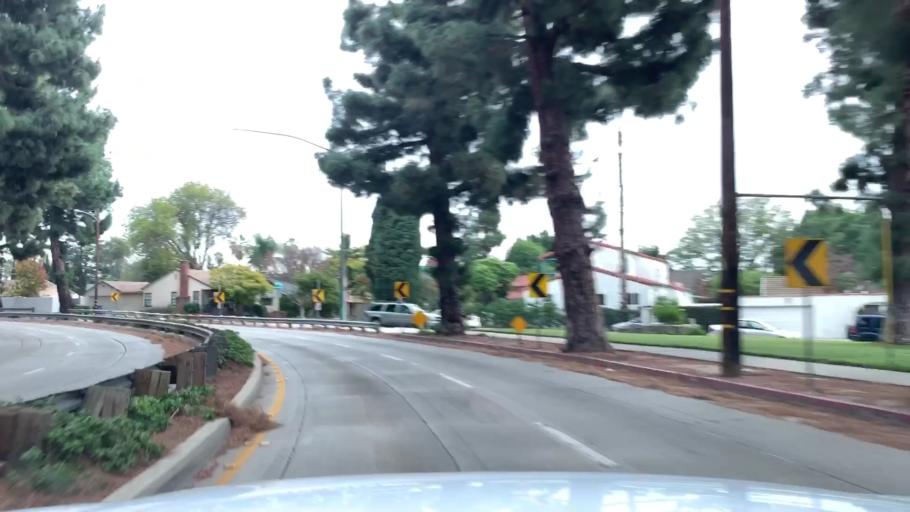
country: US
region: California
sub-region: Los Angeles County
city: Whittier
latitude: 33.9886
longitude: -118.0486
